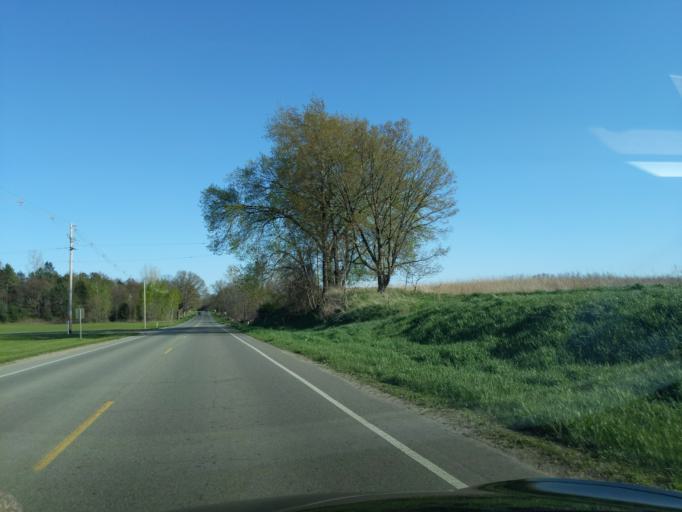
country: US
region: Michigan
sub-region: Ionia County
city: Portland
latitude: 42.8556
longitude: -84.8812
